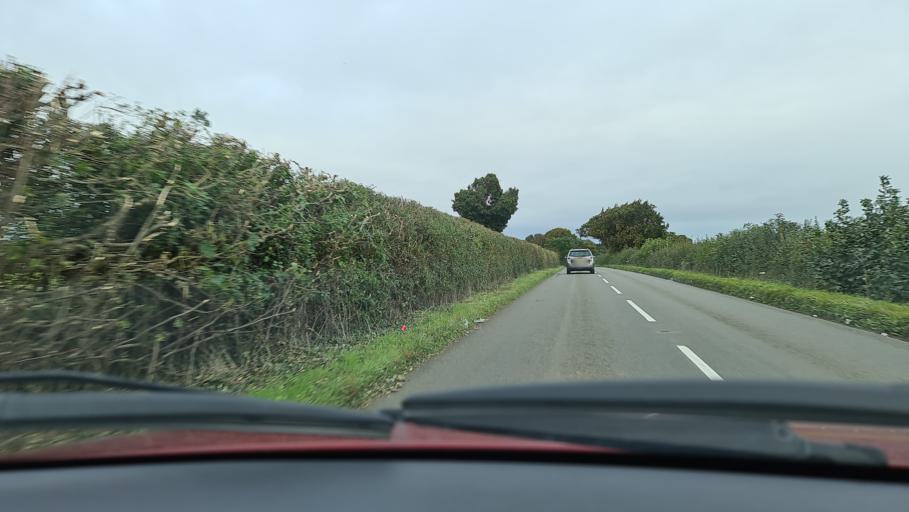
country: GB
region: England
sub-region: Oxfordshire
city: Somerton
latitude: 51.9175
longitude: -1.2388
